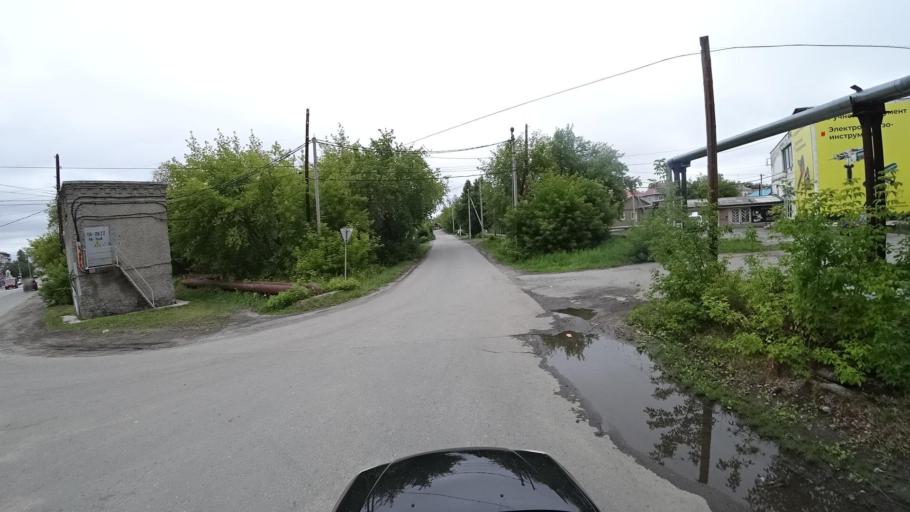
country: RU
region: Sverdlovsk
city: Kamyshlov
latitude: 56.8435
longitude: 62.7201
